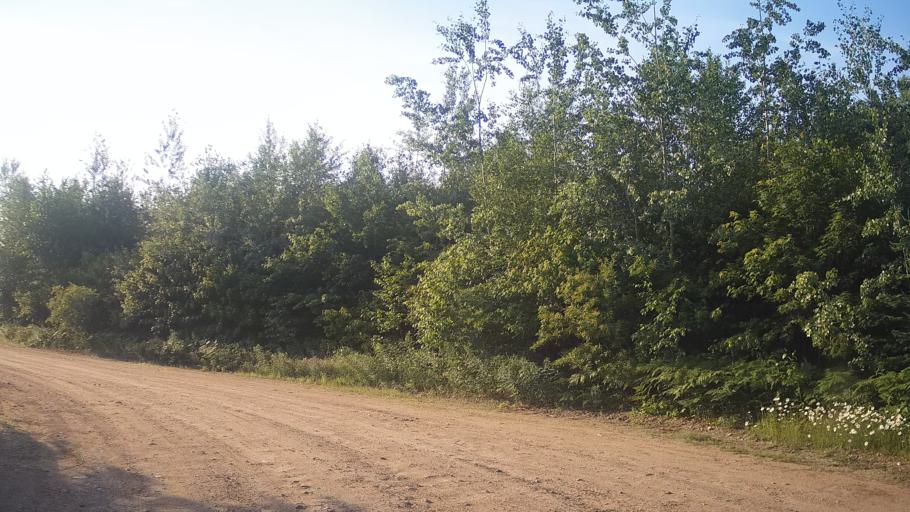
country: CA
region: Ontario
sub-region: Rainy River District
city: Atikokan
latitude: 49.4041
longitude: -91.6258
